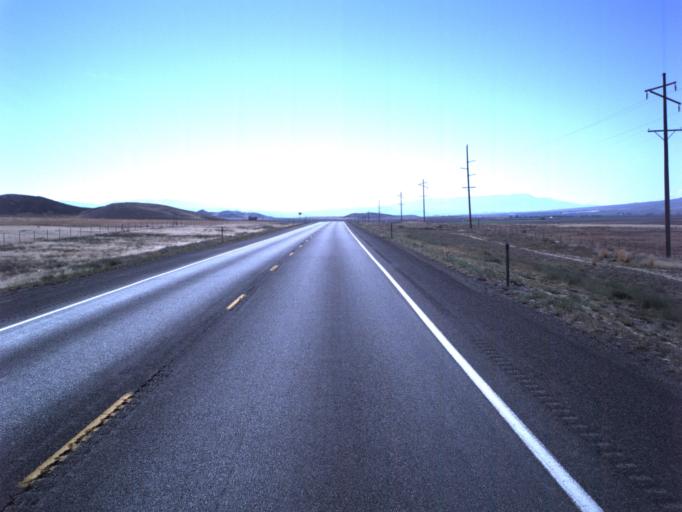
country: US
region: Utah
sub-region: Sanpete County
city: Gunnison
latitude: 39.2191
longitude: -111.8482
